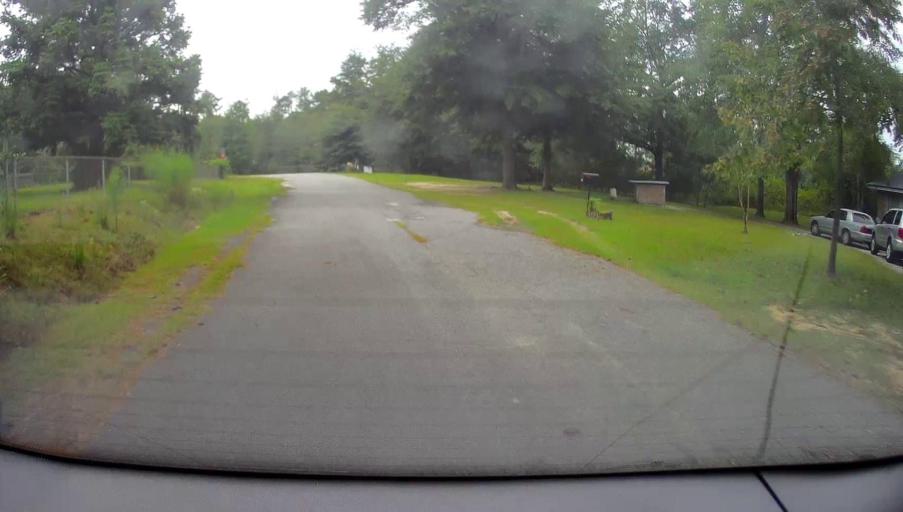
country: US
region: Georgia
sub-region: Peach County
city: Byron
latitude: 32.6792
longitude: -83.7133
